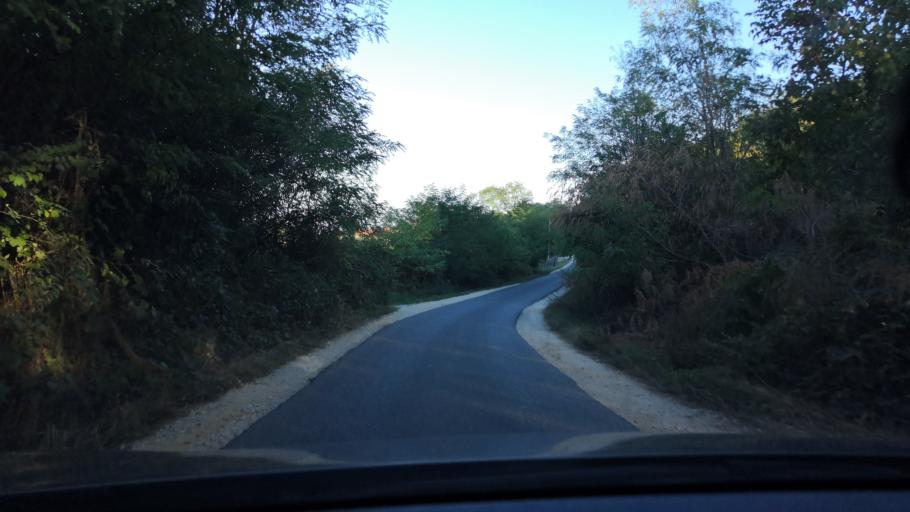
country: RS
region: Central Serbia
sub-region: Sumadijski Okrug
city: Arangelovac
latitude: 44.3305
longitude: 20.5771
